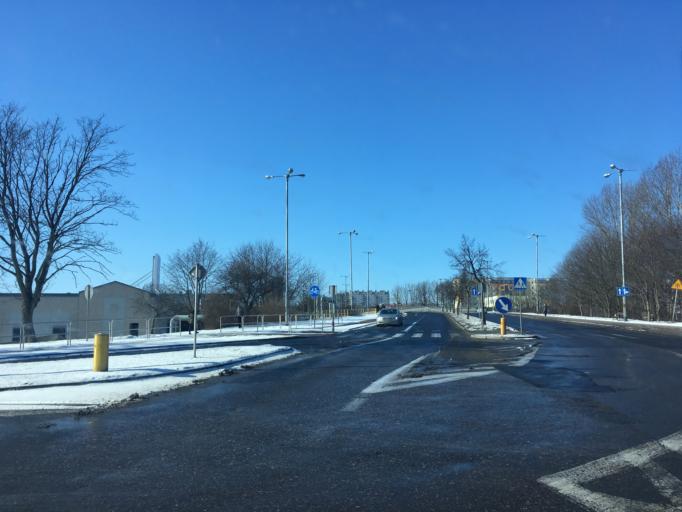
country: PL
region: Pomeranian Voivodeship
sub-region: Slupsk
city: Slupsk
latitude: 54.4721
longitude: 17.0195
